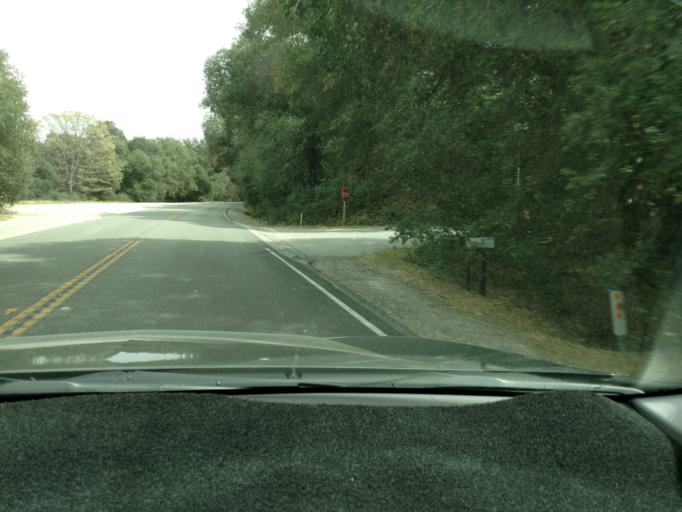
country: US
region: California
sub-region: San Diego County
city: Julian
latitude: 33.2171
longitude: -116.7441
